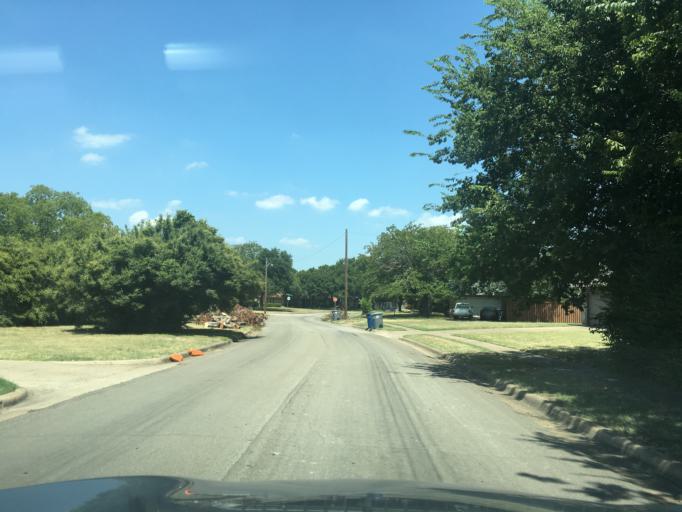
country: US
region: Texas
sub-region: Dallas County
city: Garland
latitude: 32.8668
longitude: -96.6880
